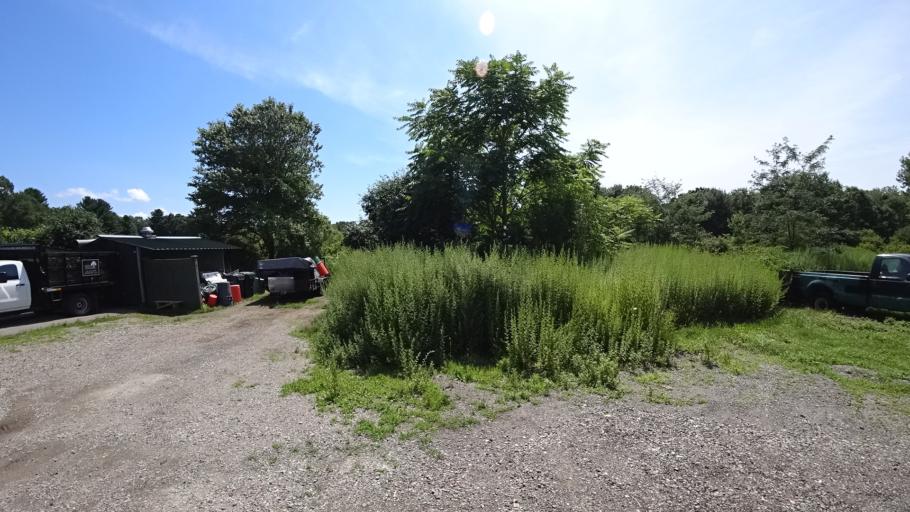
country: US
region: Massachusetts
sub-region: Norfolk County
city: Dedham
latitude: 42.2685
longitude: -71.1883
